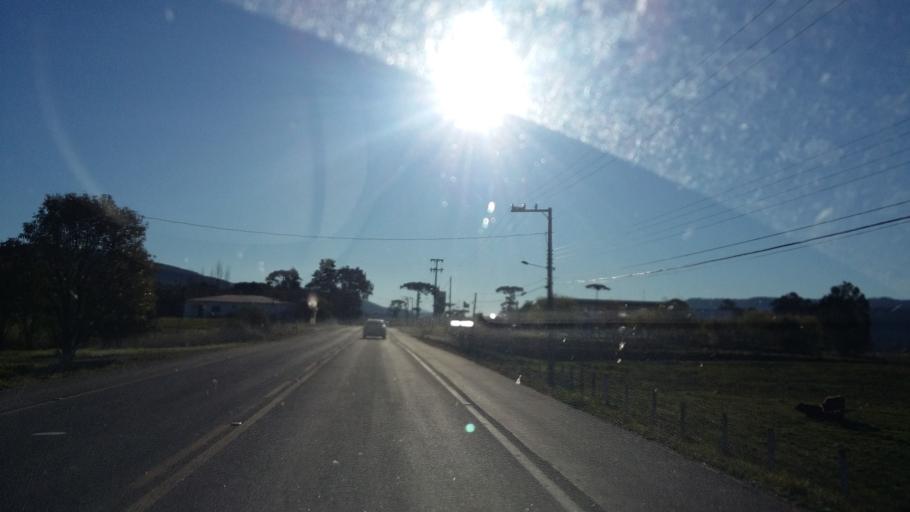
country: BR
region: Santa Catarina
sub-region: Lauro Muller
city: Lauro Muller
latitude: -27.9941
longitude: -49.5693
